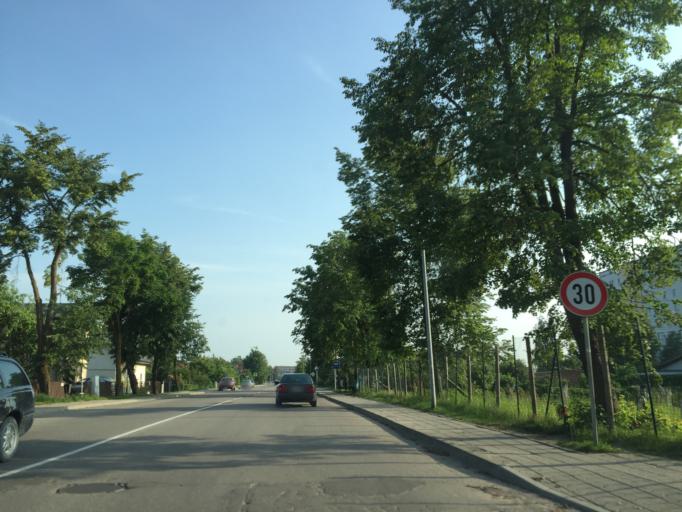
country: LV
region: Jelgava
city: Jelgava
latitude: 56.6552
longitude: 23.6983
